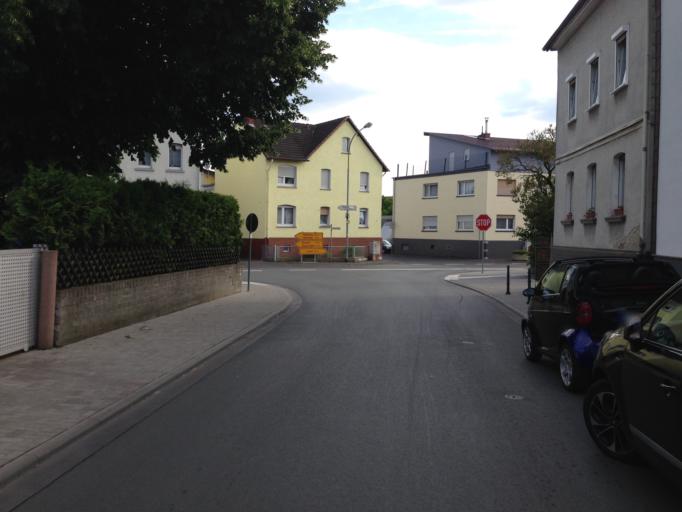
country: DE
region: Hesse
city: Staufenberg
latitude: 50.6610
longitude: 8.7271
